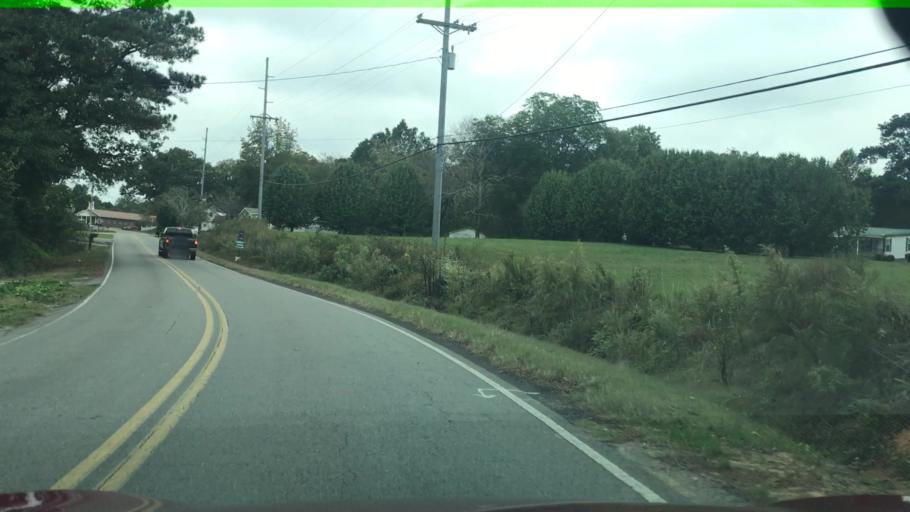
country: US
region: Alabama
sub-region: Cullman County
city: Good Hope
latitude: 34.0964
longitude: -87.0570
